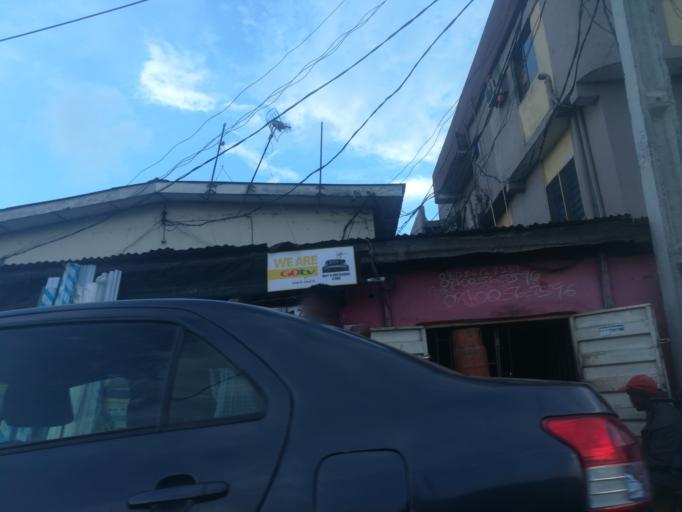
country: NG
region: Lagos
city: Somolu
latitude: 6.5594
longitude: 3.3698
